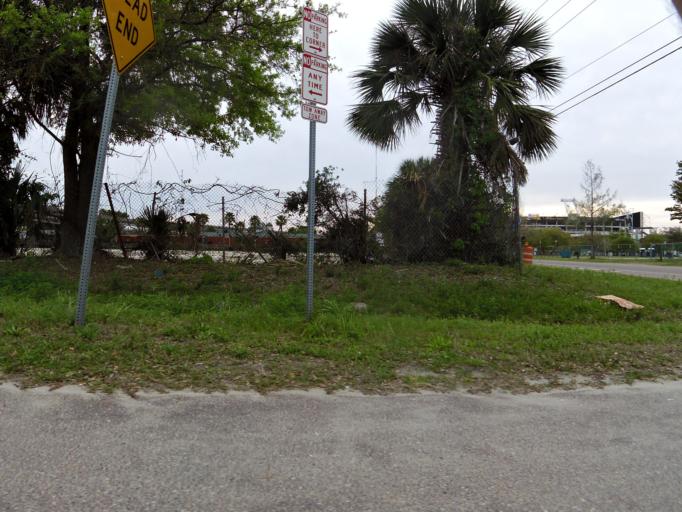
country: US
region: Florida
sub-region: Duval County
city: Jacksonville
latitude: 30.3217
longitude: -81.6313
